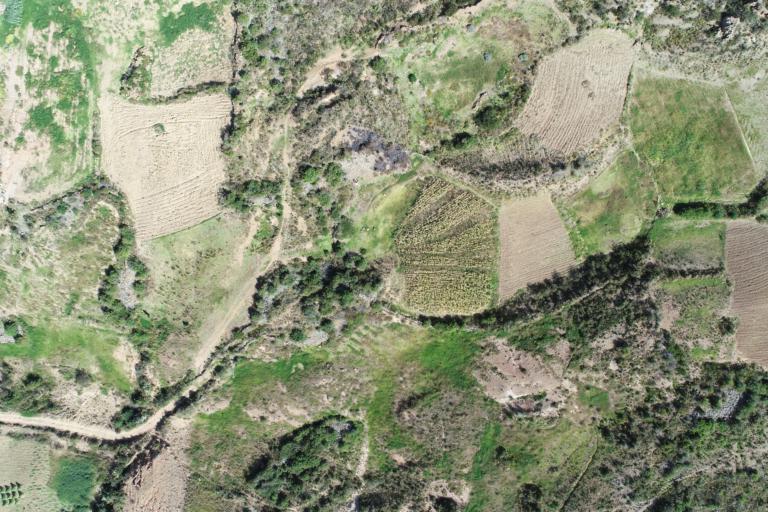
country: BO
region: La Paz
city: La Paz
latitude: -16.5576
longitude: -67.9881
